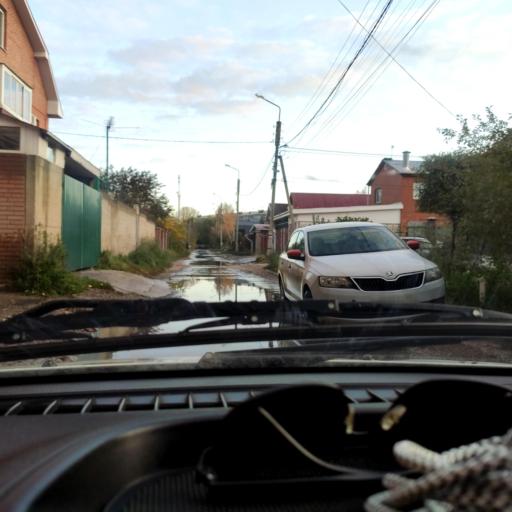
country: RU
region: Samara
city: Tol'yatti
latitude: 53.5295
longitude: 49.4246
